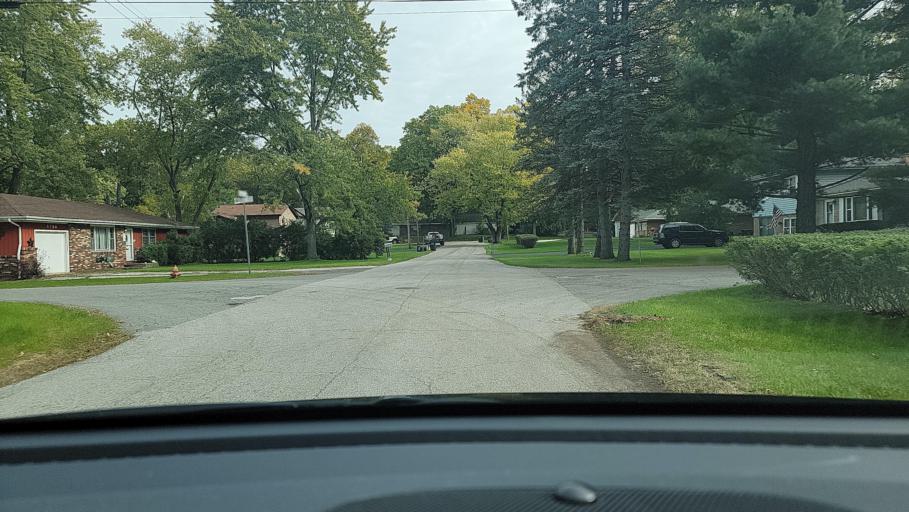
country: US
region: Indiana
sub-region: Porter County
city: Portage
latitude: 41.5778
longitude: -87.1918
